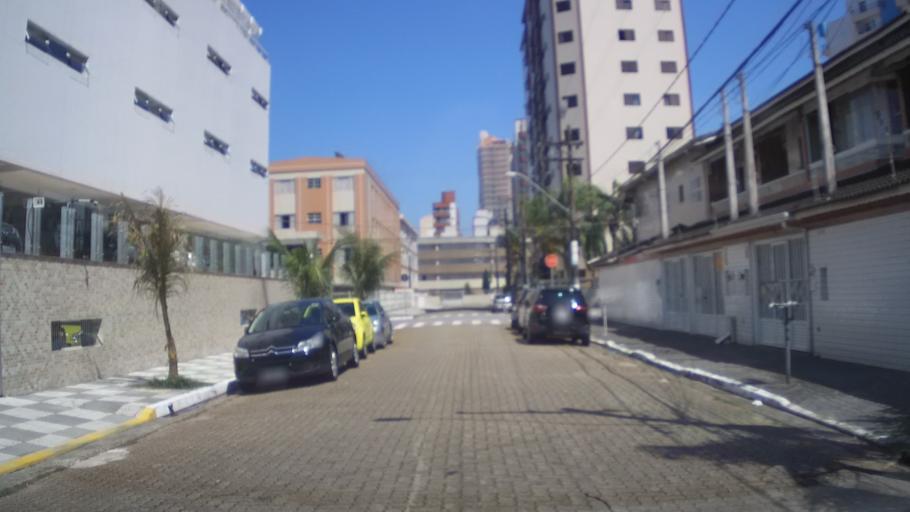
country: BR
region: Sao Paulo
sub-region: Praia Grande
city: Praia Grande
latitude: -24.0084
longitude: -46.4196
